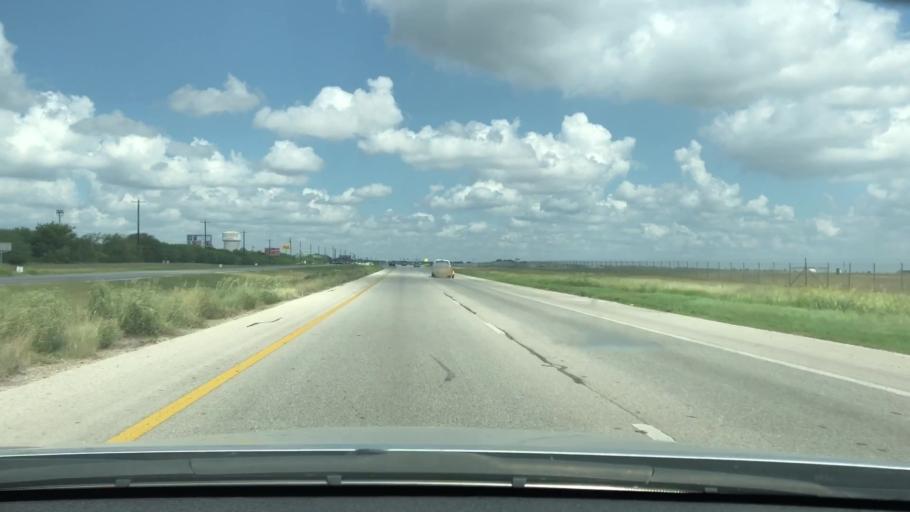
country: US
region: Texas
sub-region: Bexar County
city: Converse
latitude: 29.5164
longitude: -98.2898
